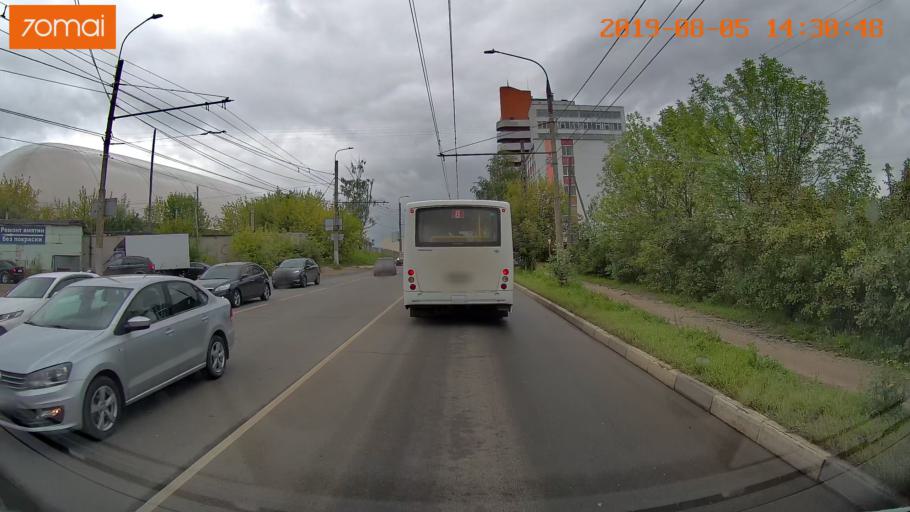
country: RU
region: Ivanovo
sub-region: Gorod Ivanovo
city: Ivanovo
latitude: 56.9850
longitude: 41.0085
